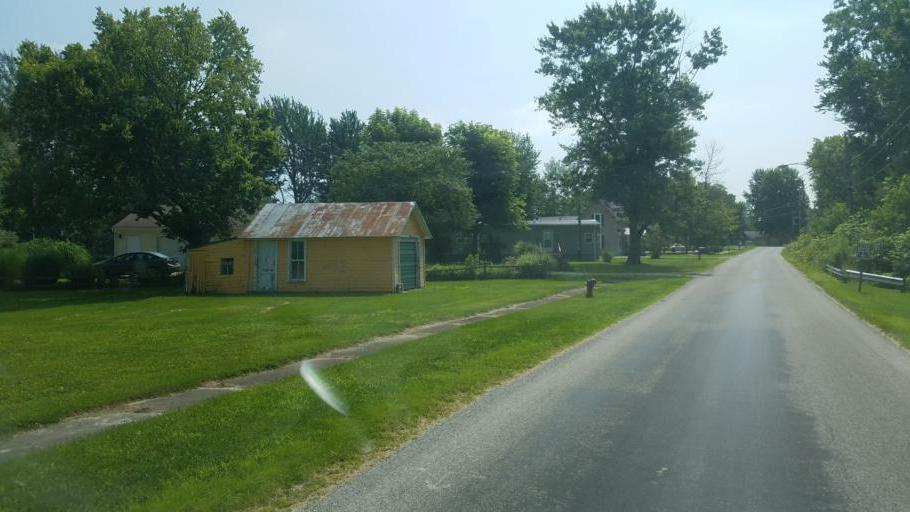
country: US
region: Ohio
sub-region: Union County
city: Richwood
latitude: 40.5821
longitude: -83.3878
